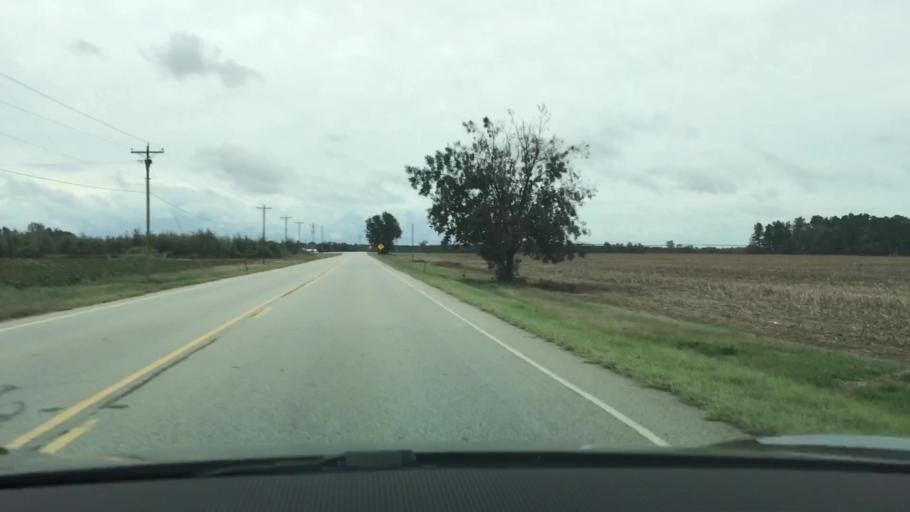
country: US
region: Georgia
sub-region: Jefferson County
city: Louisville
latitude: 33.1055
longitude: -82.4251
